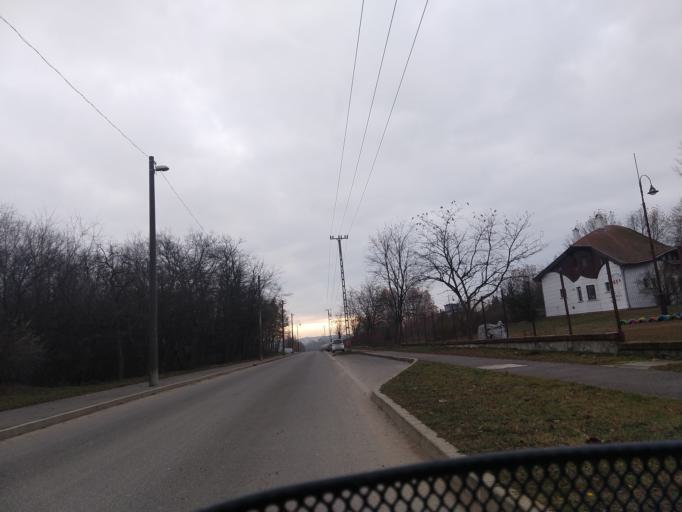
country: HU
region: Pest
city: Orbottyan
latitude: 47.6641
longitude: 19.2708
